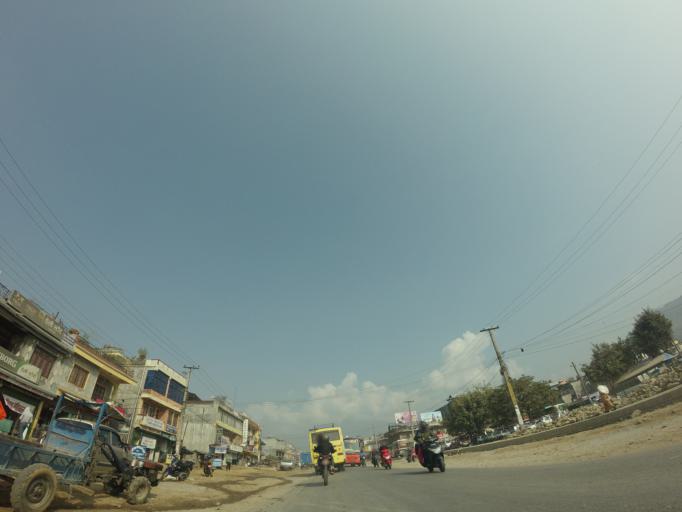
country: NP
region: Western Region
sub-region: Gandaki Zone
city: Pokhara
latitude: 28.2318
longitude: 83.9825
